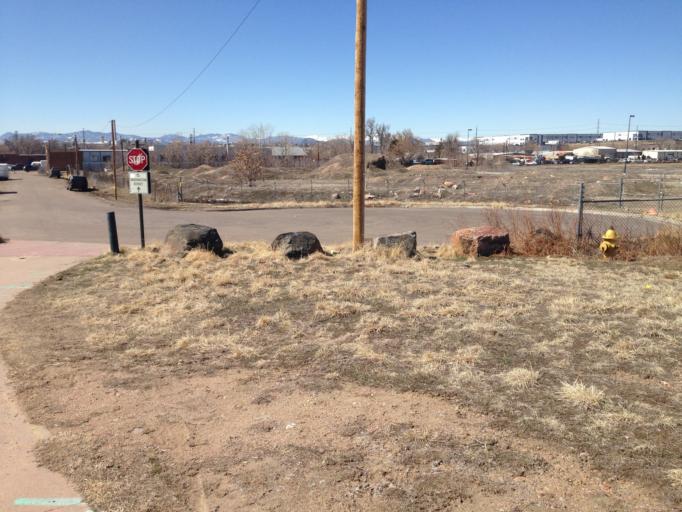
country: US
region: Colorado
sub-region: Adams County
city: Commerce City
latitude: 39.7880
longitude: -104.9737
